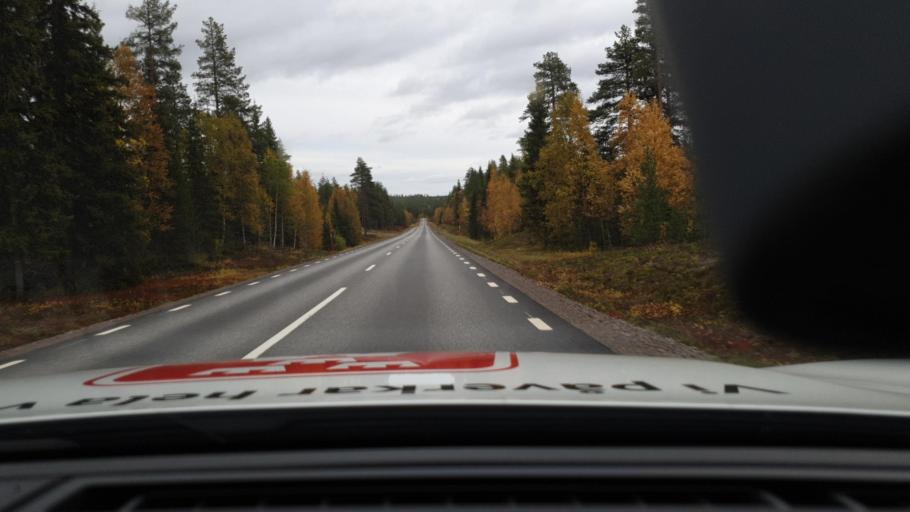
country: SE
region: Vaesterbotten
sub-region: Norsjo Kommun
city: Norsjoe
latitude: 65.4146
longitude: 19.8520
